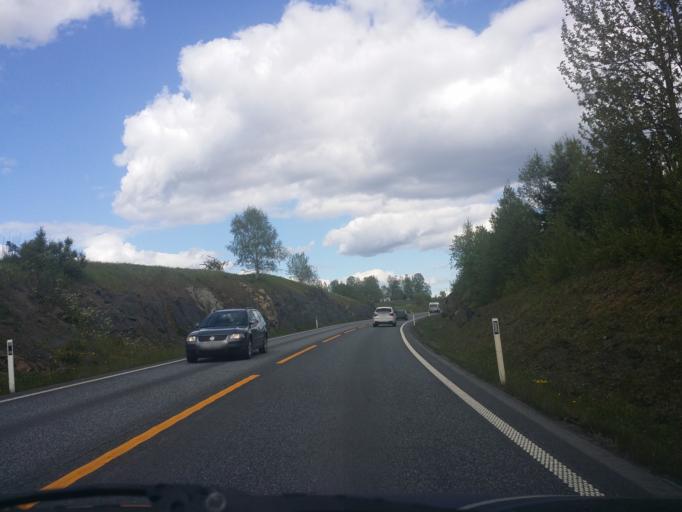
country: NO
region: Oppland
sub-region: Lunner
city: Roa
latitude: 60.2828
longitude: 10.5312
